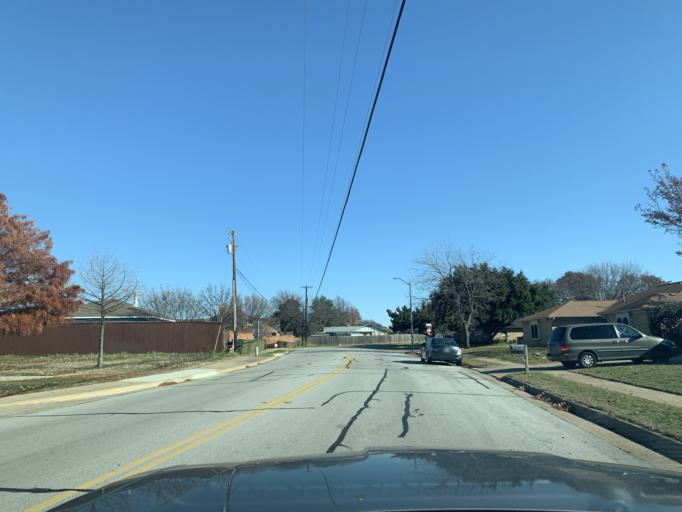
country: US
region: Texas
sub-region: Tarrant County
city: Bedford
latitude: 32.8306
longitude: -97.1398
